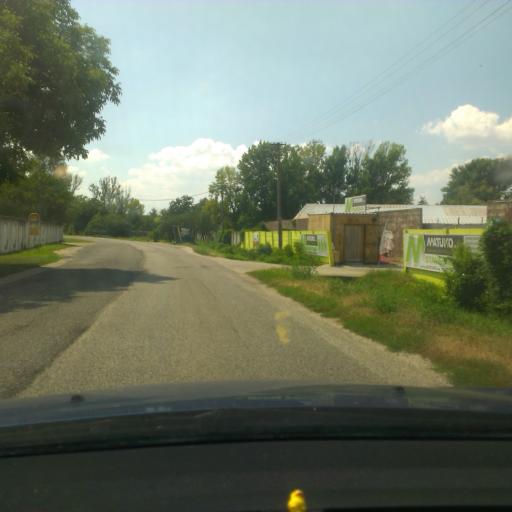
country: SK
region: Trnavsky
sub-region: Okres Trnava
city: Piestany
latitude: 48.5361
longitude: 17.8356
